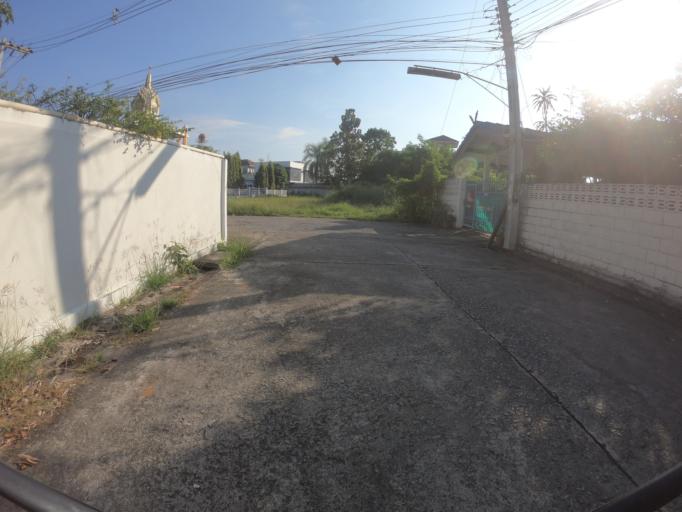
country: TH
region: Chiang Mai
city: Chiang Mai
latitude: 18.7770
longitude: 98.9793
